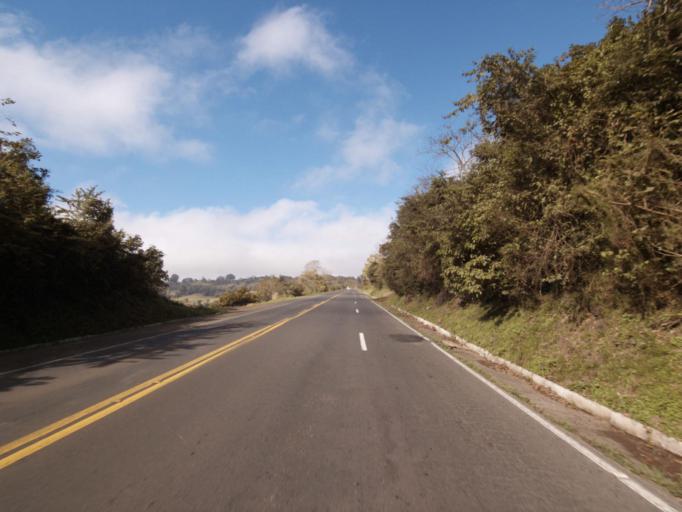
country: BR
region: Rio Grande do Sul
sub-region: Frederico Westphalen
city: Frederico Westphalen
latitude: -27.0906
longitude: -53.2194
